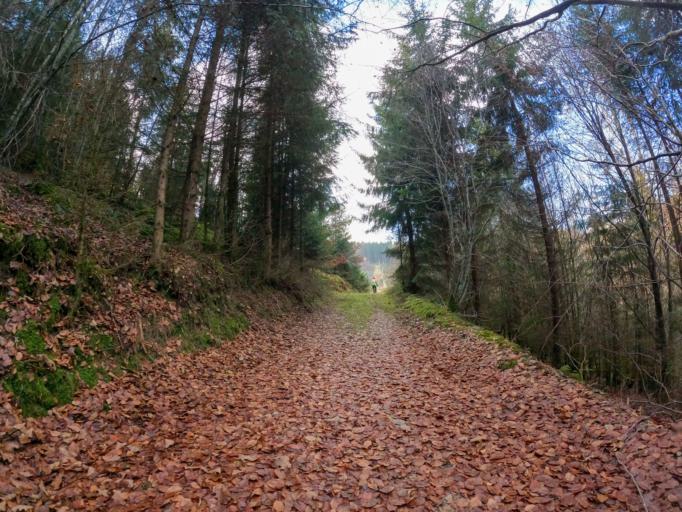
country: LU
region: Diekirch
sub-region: Canton de Wiltz
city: Winseler
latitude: 49.9892
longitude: 5.8414
